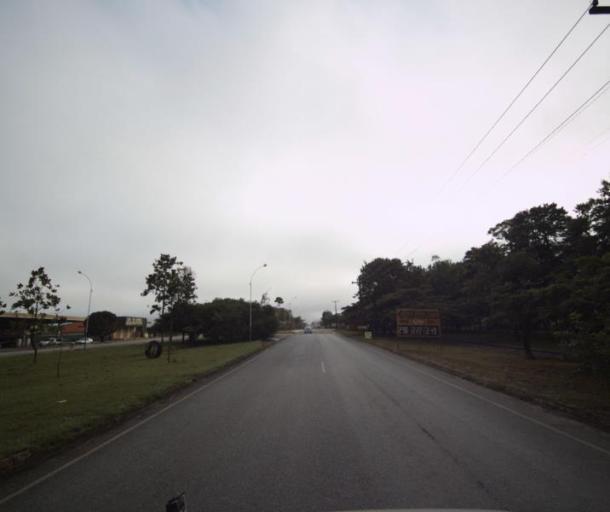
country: BR
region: Goias
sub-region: Pirenopolis
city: Pirenopolis
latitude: -15.7889
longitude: -48.7716
